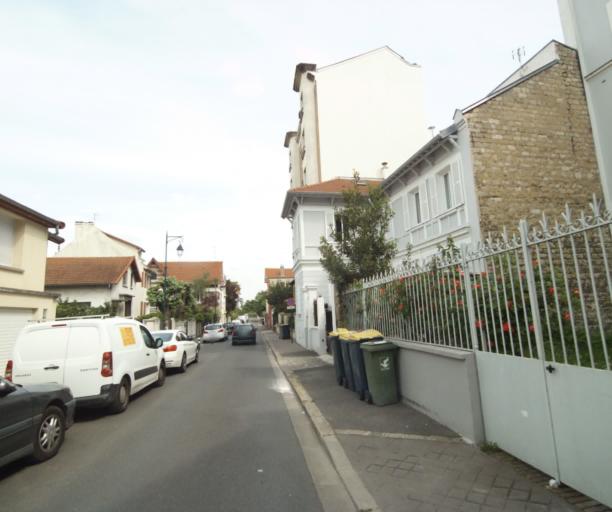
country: FR
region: Ile-de-France
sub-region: Departement des Hauts-de-Seine
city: Colombes
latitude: 48.9214
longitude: 2.2594
